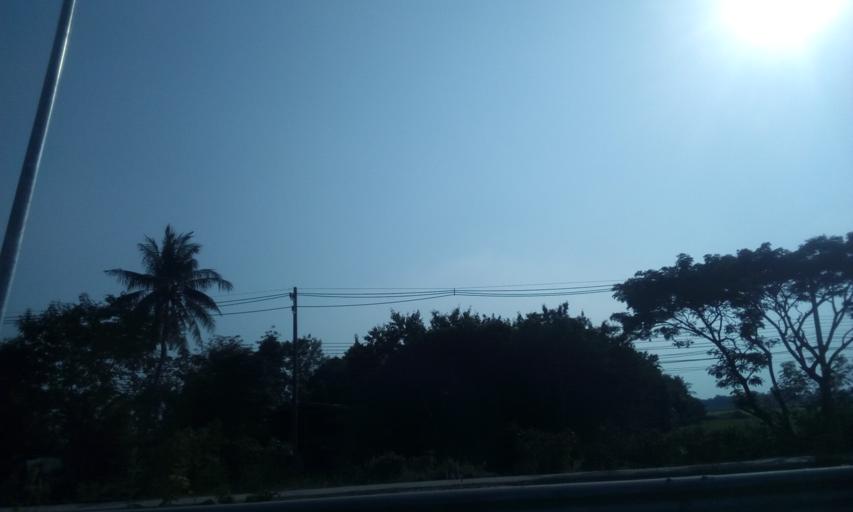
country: TH
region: Sing Buri
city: Sing Buri
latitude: 14.8440
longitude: 100.4247
